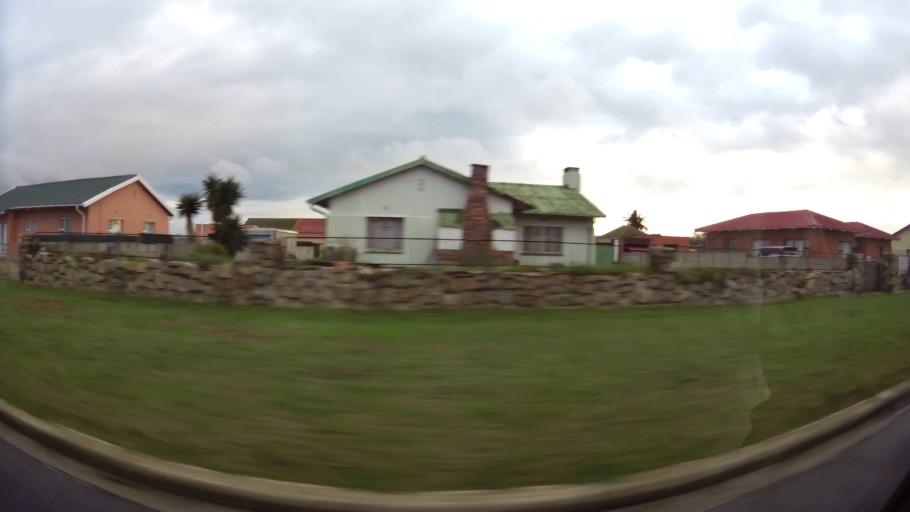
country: ZA
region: Eastern Cape
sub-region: Nelson Mandela Bay Metropolitan Municipality
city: Port Elizabeth
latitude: -33.9230
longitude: 25.6017
